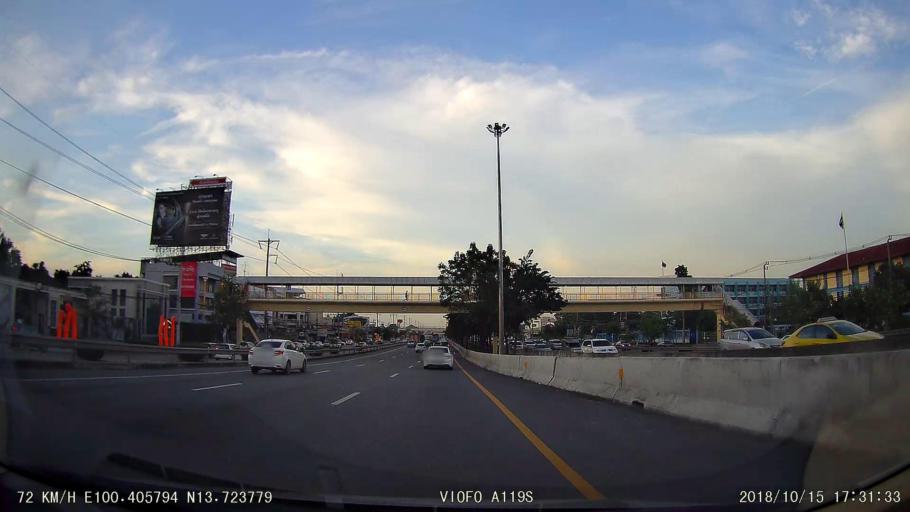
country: TH
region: Bangkok
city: Bang Khae
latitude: 13.7239
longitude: 100.4058
